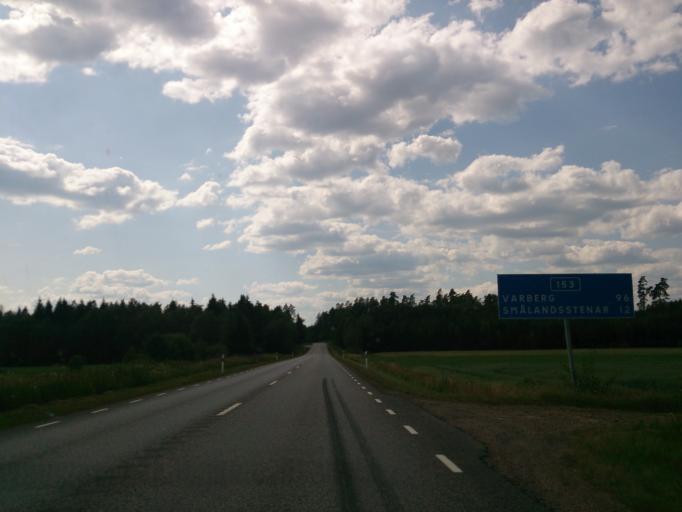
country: SE
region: Joenkoeping
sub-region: Gislaveds Kommun
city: Reftele
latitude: 57.1715
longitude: 13.5862
